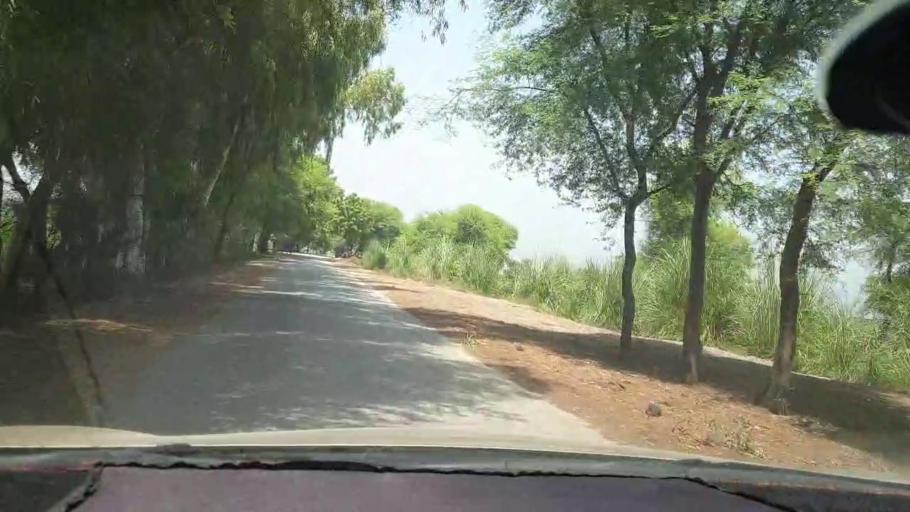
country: PK
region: Sindh
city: Kambar
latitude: 27.6606
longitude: 67.9487
